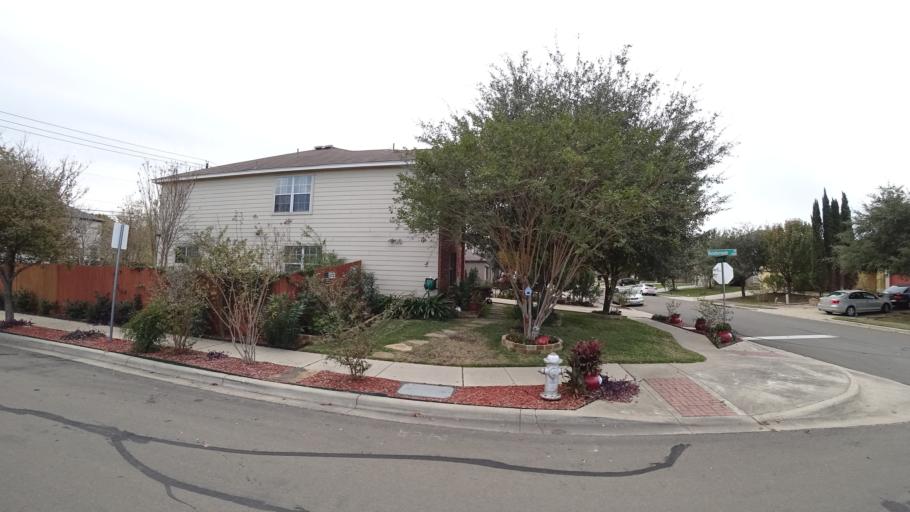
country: US
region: Texas
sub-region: Travis County
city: Onion Creek
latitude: 30.1596
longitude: -97.7400
